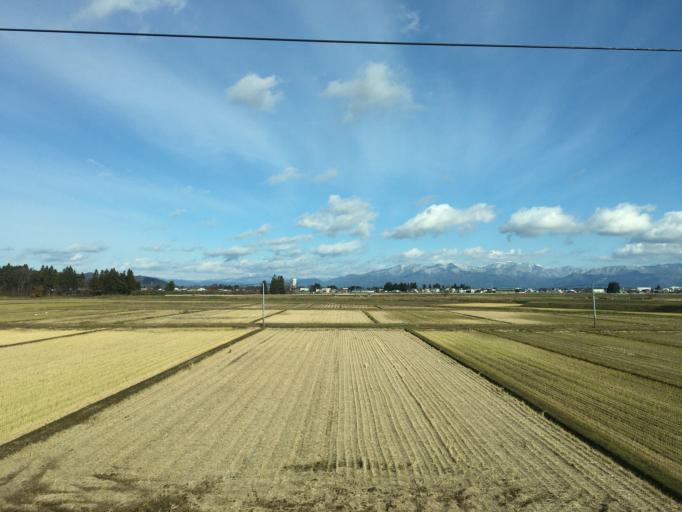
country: JP
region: Akita
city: Omagari
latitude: 39.4783
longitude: 140.4667
